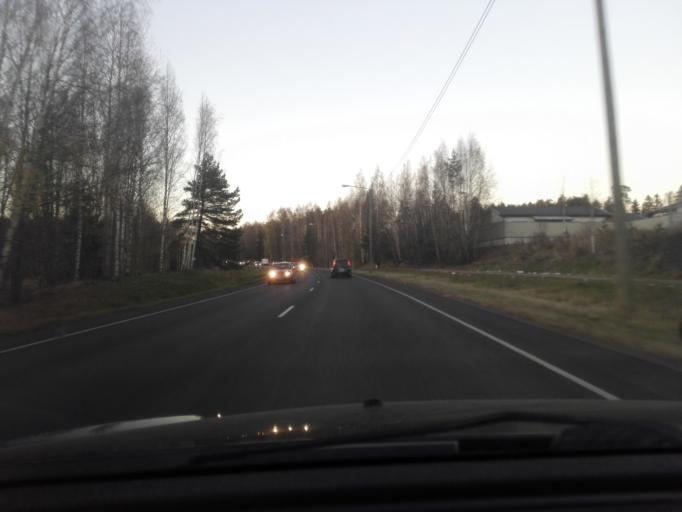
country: FI
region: Uusimaa
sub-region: Helsinki
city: Vantaa
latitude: 60.2847
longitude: 25.1037
